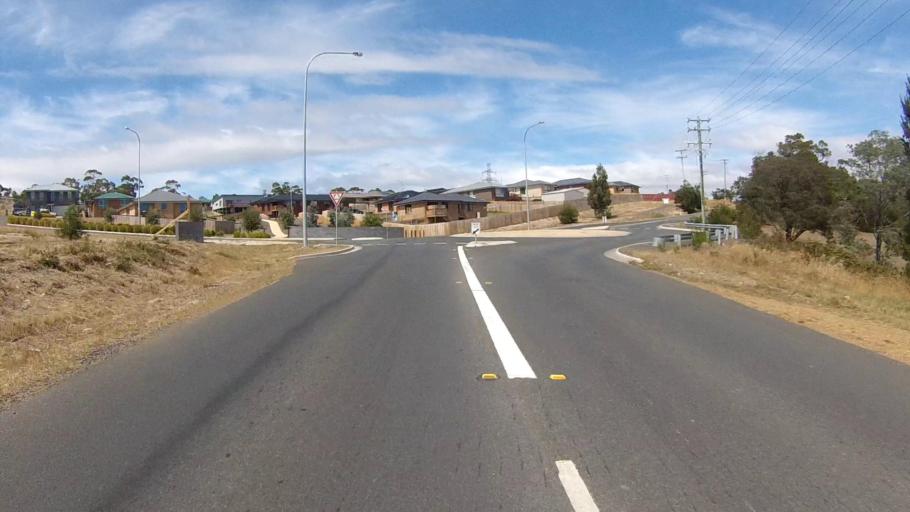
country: AU
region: Tasmania
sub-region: Clarence
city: Lindisfarne
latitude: -42.8203
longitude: 147.3512
